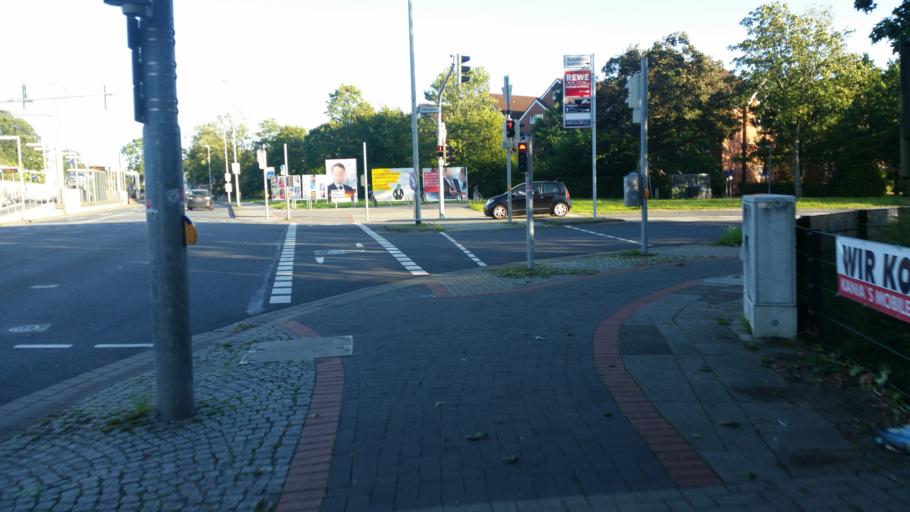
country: DE
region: Lower Saxony
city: Isernhagen Farster Bauerschaft
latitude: 52.3998
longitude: 9.8294
